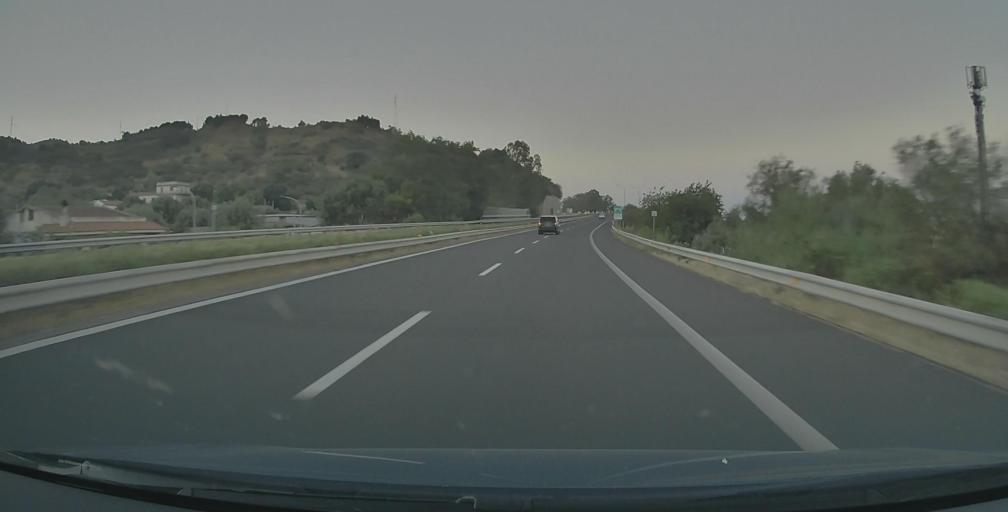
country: IT
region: Sicily
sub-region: Messina
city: Roccalumera
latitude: 37.9822
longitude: 15.3991
